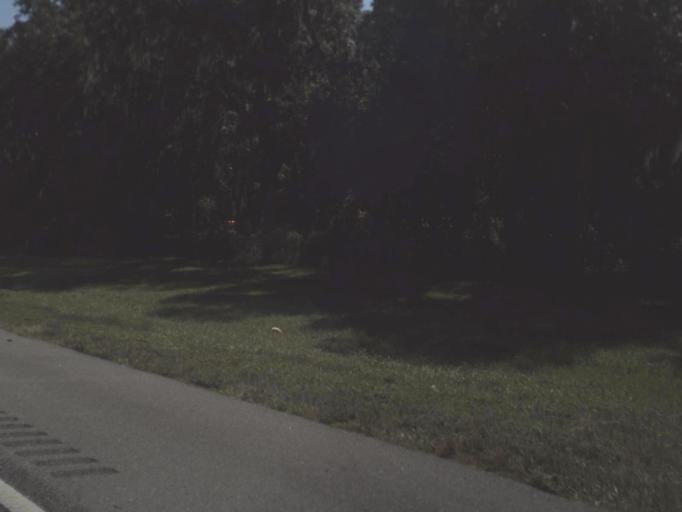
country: US
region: Florida
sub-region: Sumter County
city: Wildwood
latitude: 28.8296
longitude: -82.0329
